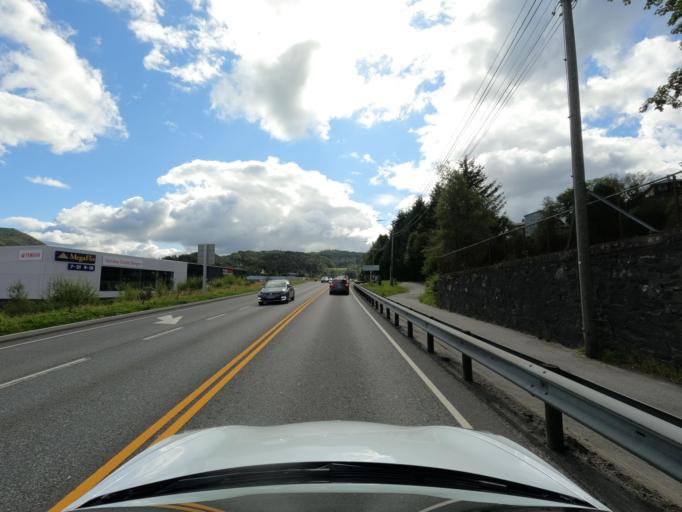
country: NO
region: Hordaland
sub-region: Bergen
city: Hylkje
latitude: 60.4876
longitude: 5.3766
